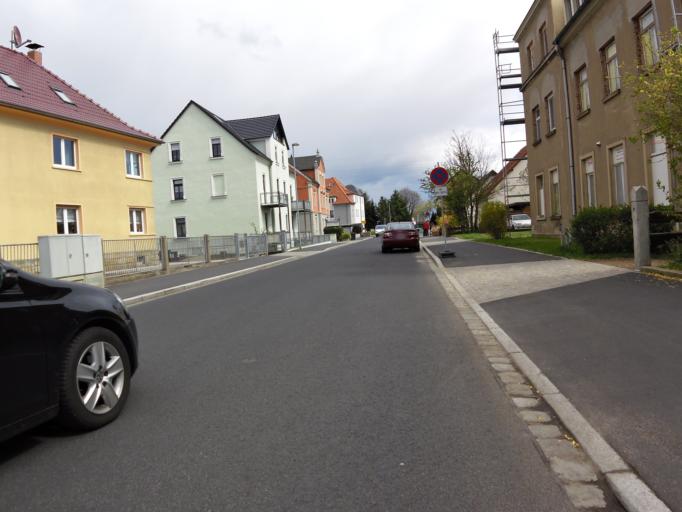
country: DE
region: Saxony
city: Coswig
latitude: 51.1148
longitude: 13.5797
